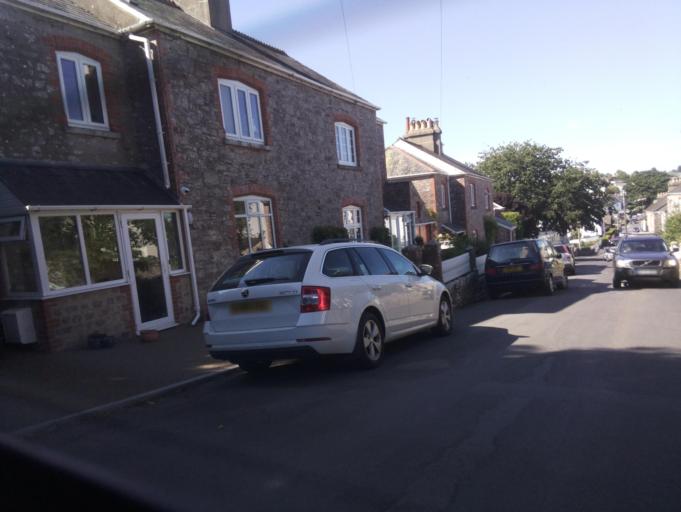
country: GB
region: England
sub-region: Borough of Torbay
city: Paignton
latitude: 50.3934
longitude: -3.5659
